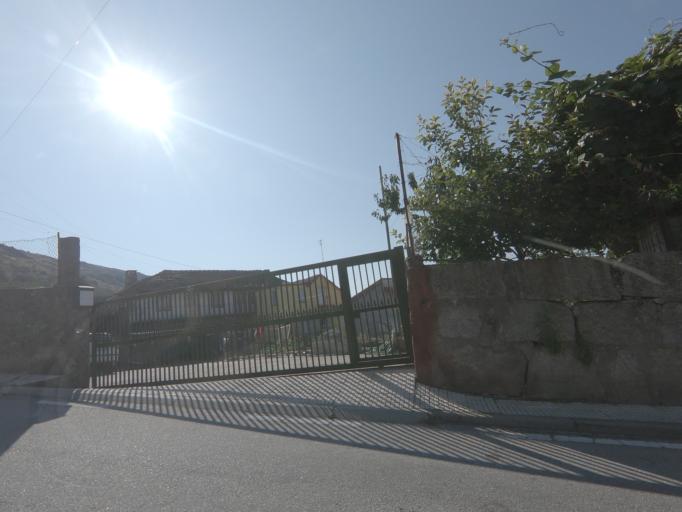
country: PT
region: Viseu
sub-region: Tabuaco
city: Tabuaco
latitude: 41.1155
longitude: -7.5705
